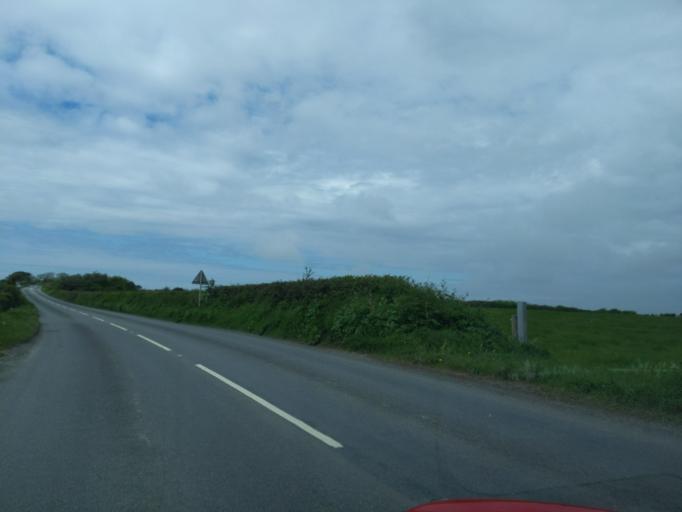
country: GB
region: England
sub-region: Cornwall
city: Wadebridge
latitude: 50.5594
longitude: -4.8639
